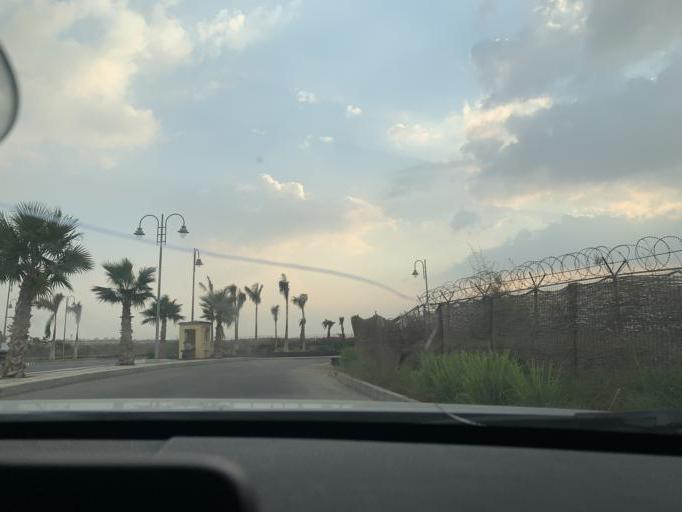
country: EG
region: Muhafazat al Qalyubiyah
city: Al Khankah
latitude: 30.0973
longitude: 31.6571
